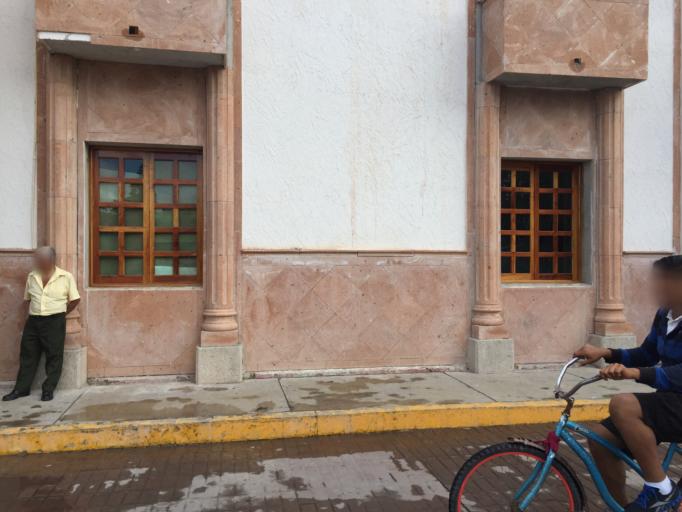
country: MX
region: Veracruz
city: Tecolutla
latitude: 20.4773
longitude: -97.0085
